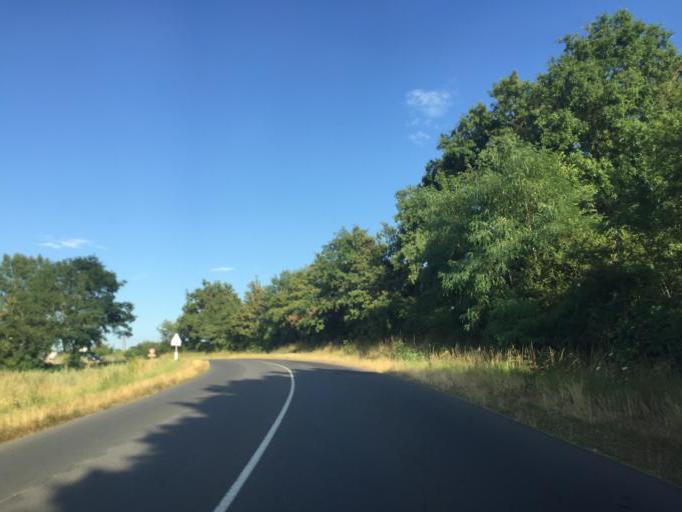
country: FR
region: Auvergne
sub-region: Departement de l'Allier
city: Toulon-sur-Allier
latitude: 46.5358
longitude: 3.3510
